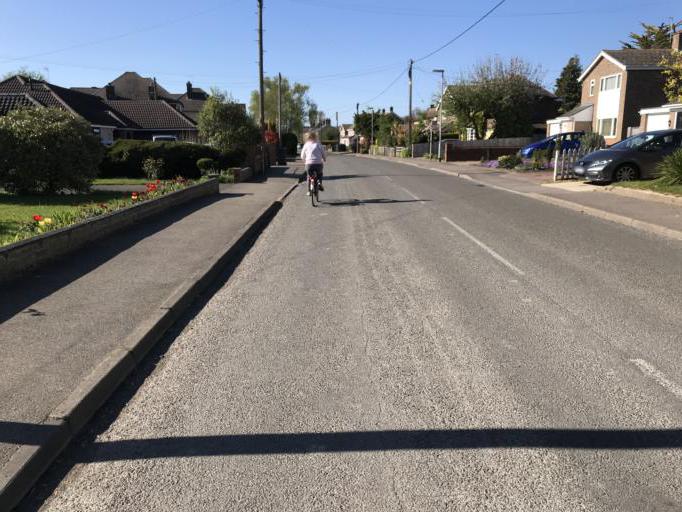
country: GB
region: England
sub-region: Cambridgeshire
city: Fulbourn
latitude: 52.1995
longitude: 0.1950
